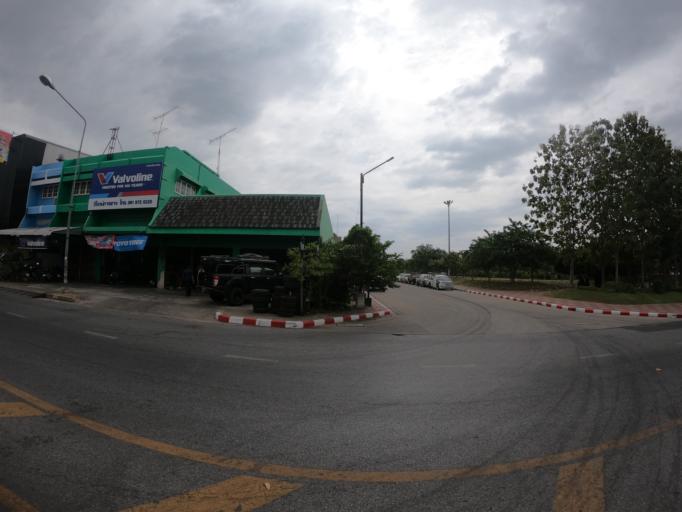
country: TH
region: Roi Et
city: Roi Et
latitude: 16.0539
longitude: 103.6439
